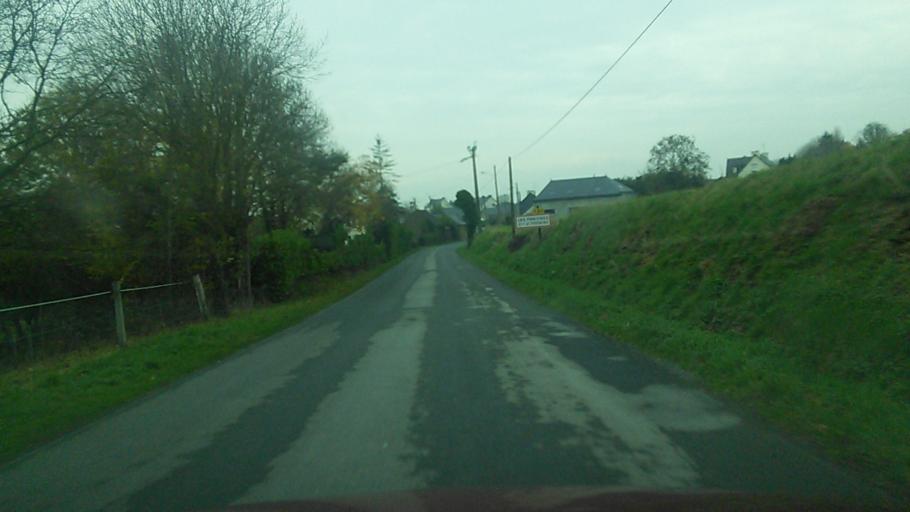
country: FR
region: Brittany
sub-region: Departement des Cotes-d'Armor
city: Yffiniac
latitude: 48.4755
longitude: -2.6556
